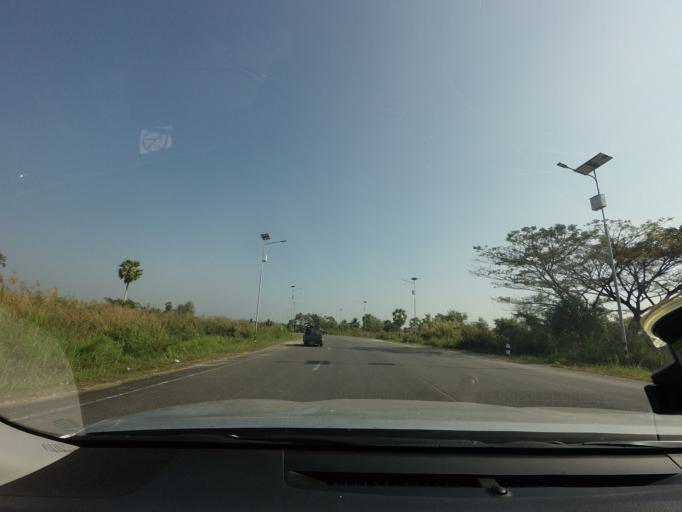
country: TH
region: Nakhon Si Thammarat
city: Nakhon Si Thammarat
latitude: 8.4677
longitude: 99.9810
